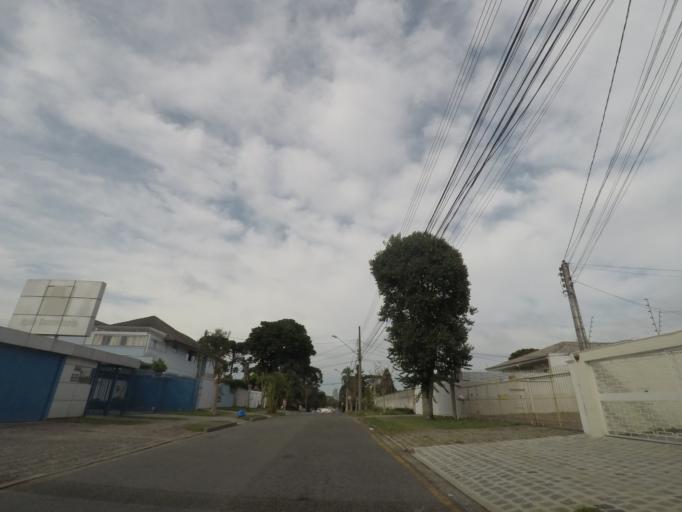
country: BR
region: Parana
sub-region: Curitiba
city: Curitiba
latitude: -25.4089
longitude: -49.2741
